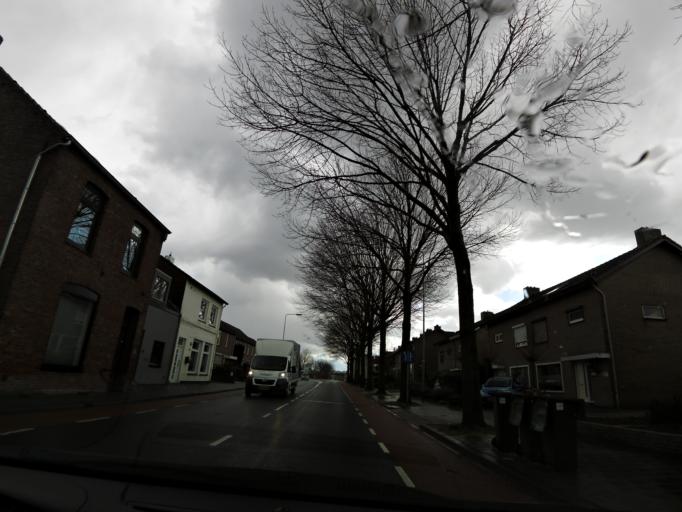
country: NL
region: Limburg
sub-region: Gemeente Sittard-Geleen
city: Limbricht
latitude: 51.0105
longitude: 5.8405
